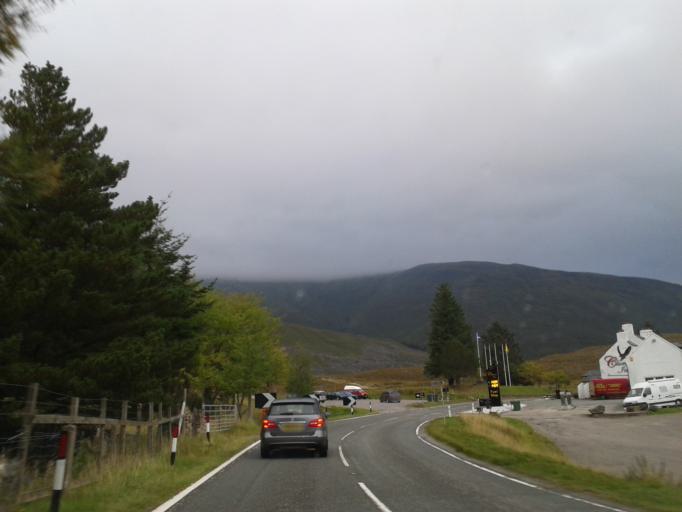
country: GB
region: Scotland
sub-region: Highland
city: Fort William
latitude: 57.1559
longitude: -5.1837
